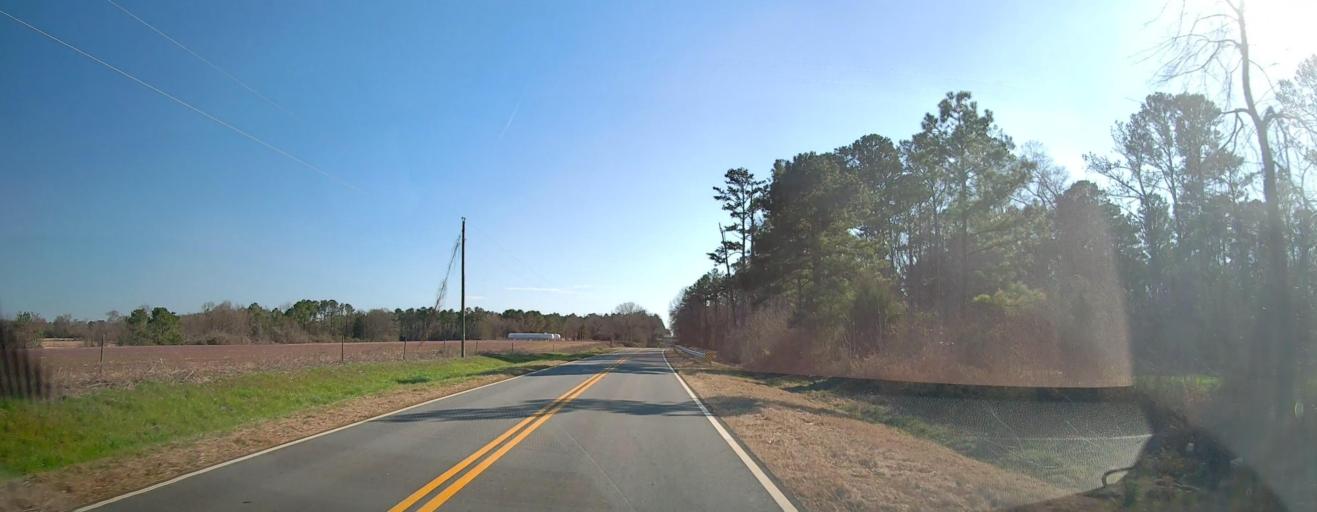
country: US
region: Georgia
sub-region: Sumter County
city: Americus
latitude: 32.0813
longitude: -84.1662
